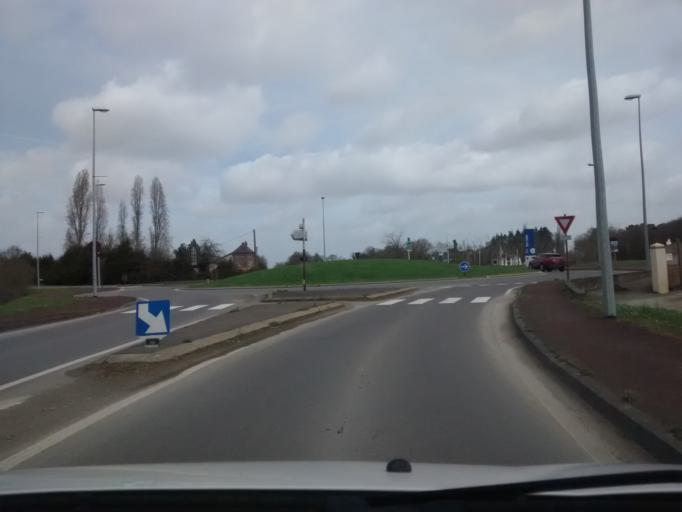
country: FR
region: Brittany
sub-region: Departement d'Ille-et-Vilaine
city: Bruz
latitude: 48.0421
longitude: -1.7542
